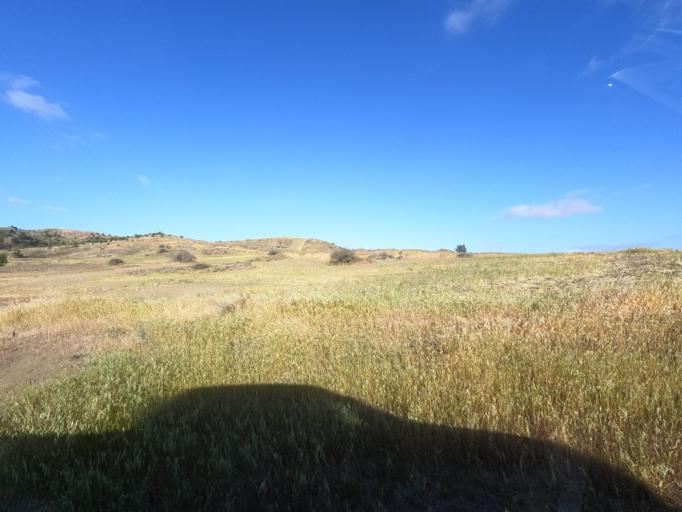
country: CY
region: Lefkosia
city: Peristerona
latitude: 35.0731
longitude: 33.0436
